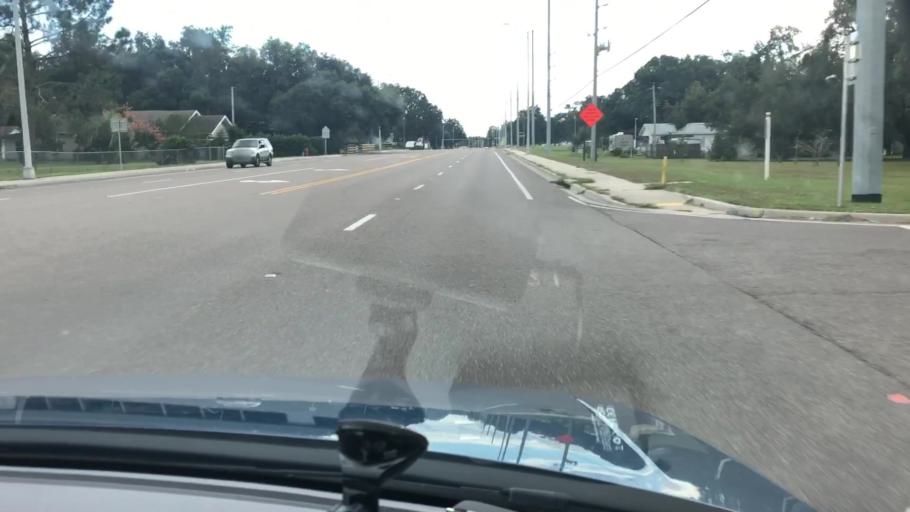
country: US
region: Florida
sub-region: Polk County
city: Kathleen
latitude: 28.1280
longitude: -82.0234
